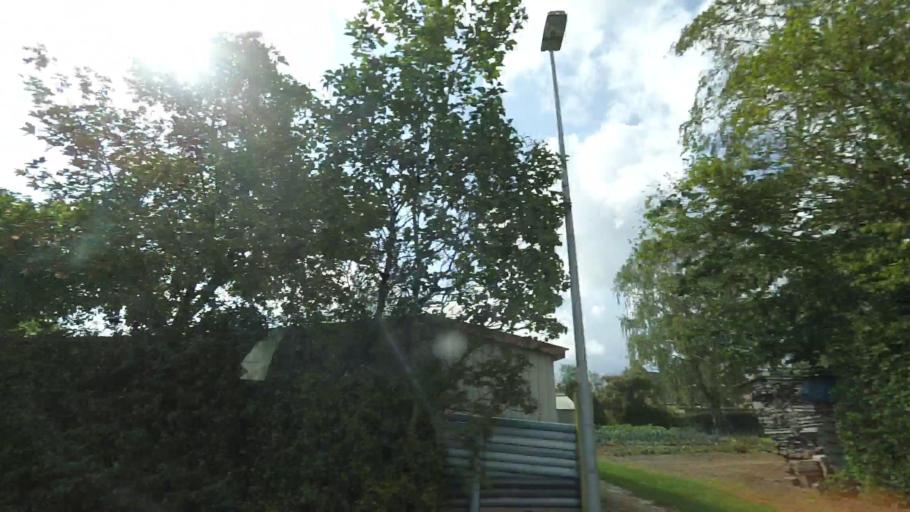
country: DK
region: Central Jutland
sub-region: Syddjurs Kommune
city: Ryomgard
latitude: 56.4774
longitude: 10.5002
